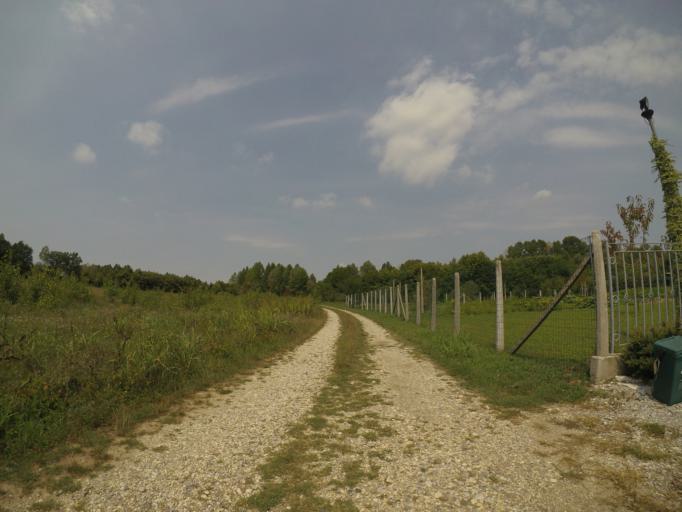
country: IT
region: Friuli Venezia Giulia
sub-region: Provincia di Udine
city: Rivignano
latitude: 45.9026
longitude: 13.0221
